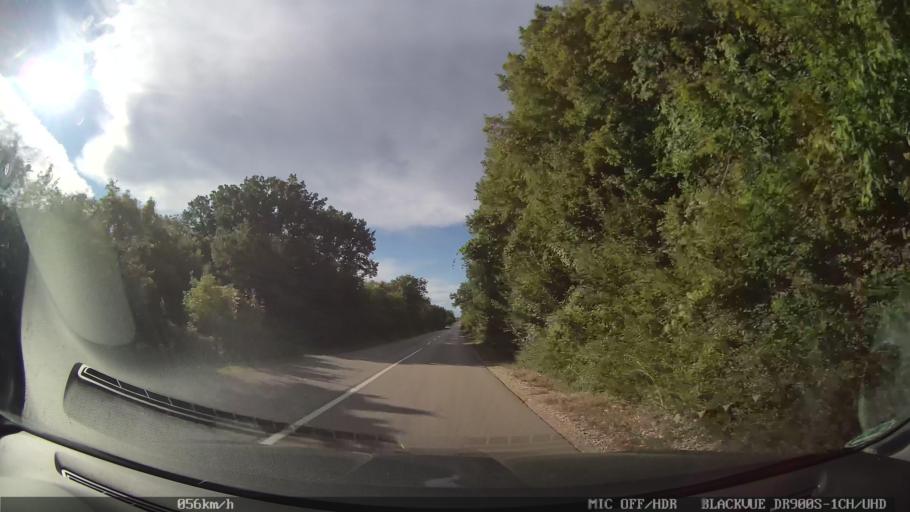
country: HR
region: Primorsko-Goranska
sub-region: Grad Krk
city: Krk
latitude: 45.0640
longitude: 14.4751
